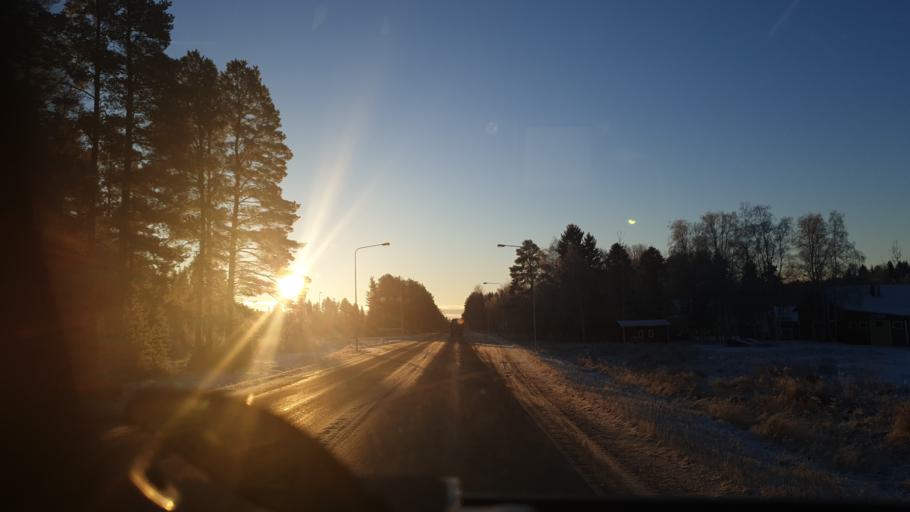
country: FI
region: Northern Ostrobothnia
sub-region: Ylivieska
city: Kalajoki
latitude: 64.2792
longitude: 23.9486
